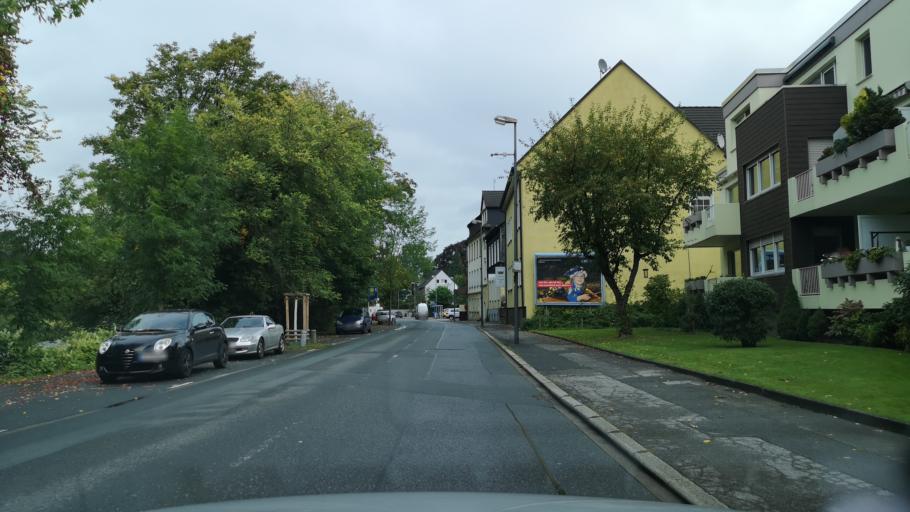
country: DE
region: North Rhine-Westphalia
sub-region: Regierungsbezirk Dusseldorf
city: Heiligenhaus
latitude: 51.3818
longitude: 7.0000
